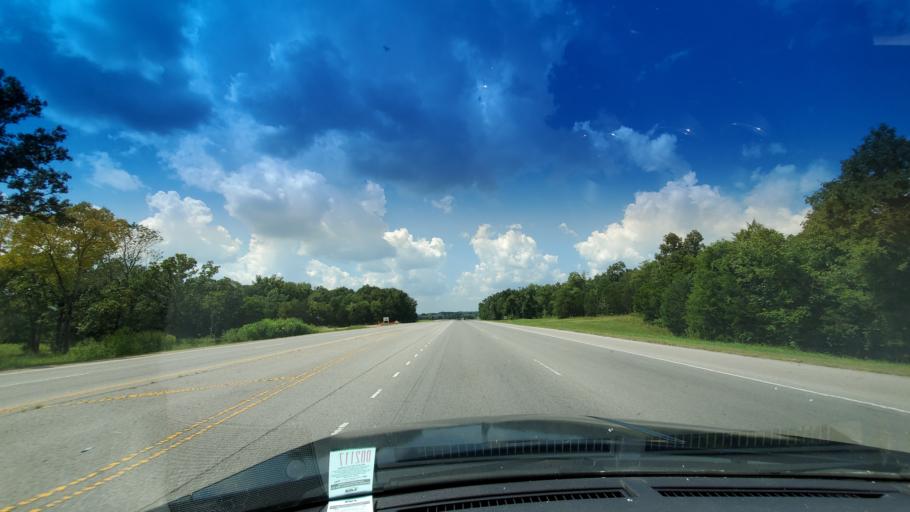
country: US
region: Tennessee
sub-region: Wilson County
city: Lebanon
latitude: 36.1758
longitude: -86.3160
